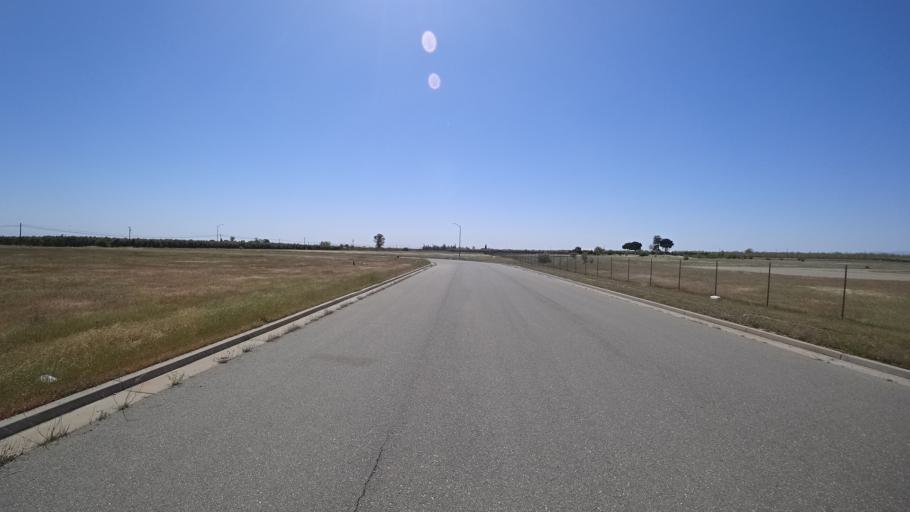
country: US
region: California
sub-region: Glenn County
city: Orland
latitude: 39.7153
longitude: -122.1431
